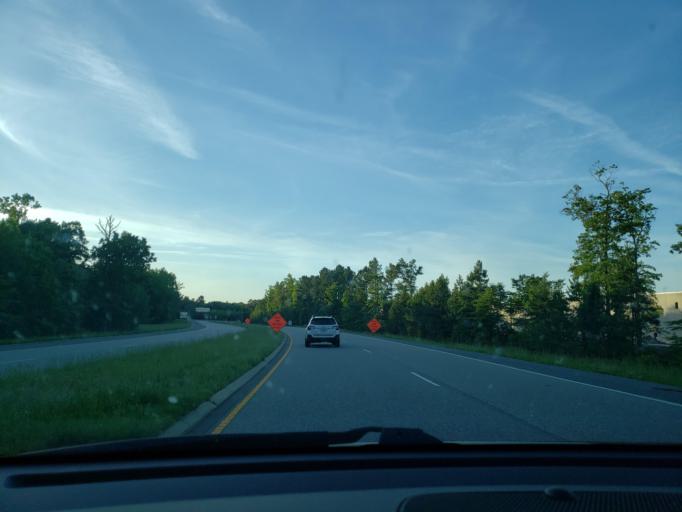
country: US
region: Virginia
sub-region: Henrico County
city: Fort Lee
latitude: 37.4827
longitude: -77.3400
